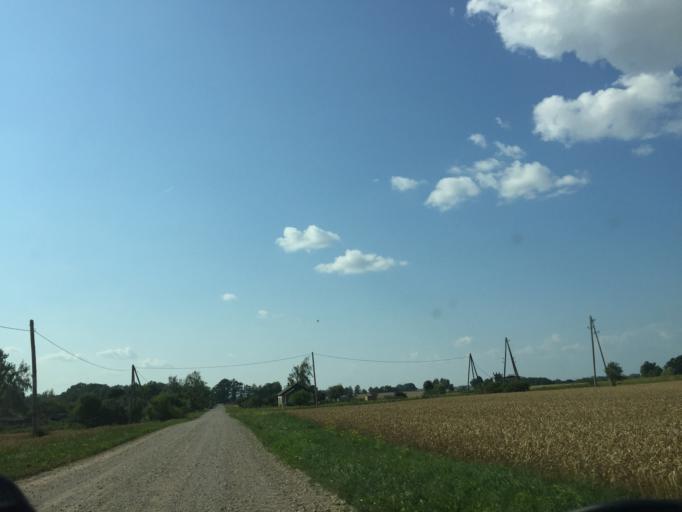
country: LV
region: Jelgava
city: Jelgava
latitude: 56.4501
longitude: 23.7464
